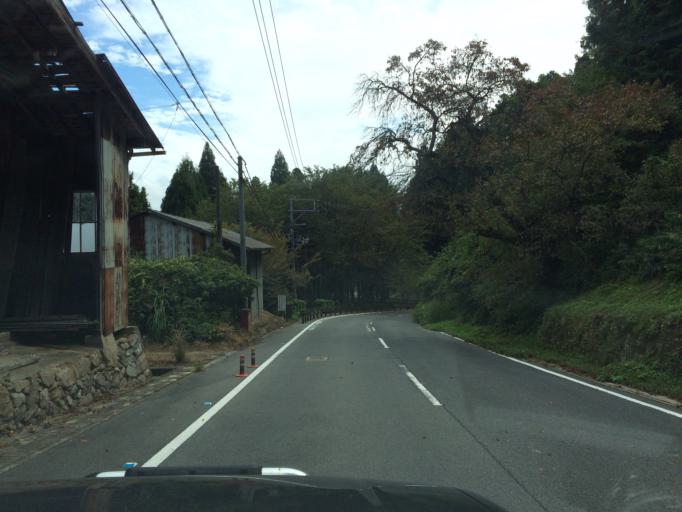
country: JP
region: Mie
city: Nabari
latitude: 34.6784
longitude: 135.9620
